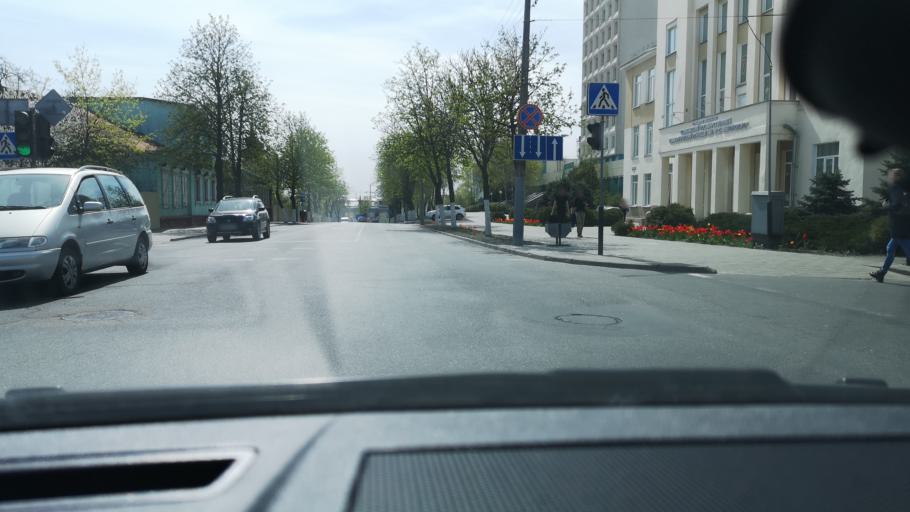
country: BY
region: Gomel
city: Gomel
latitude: 52.4163
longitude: 31.0068
